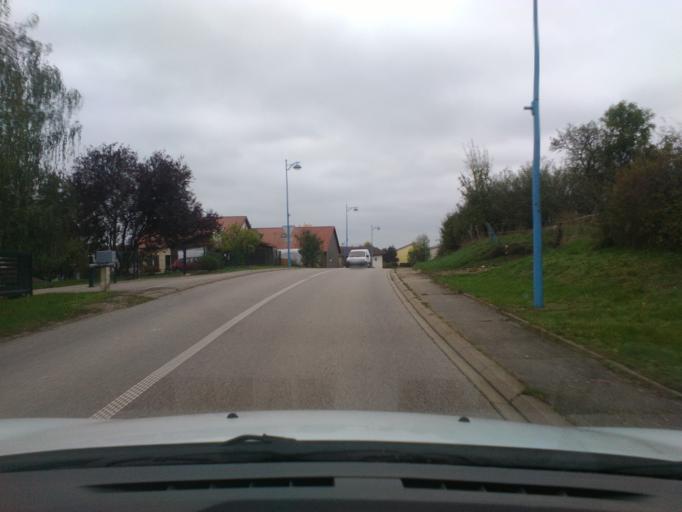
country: FR
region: Lorraine
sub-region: Departement des Vosges
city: Aydoilles
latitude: 48.2585
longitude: 6.5357
